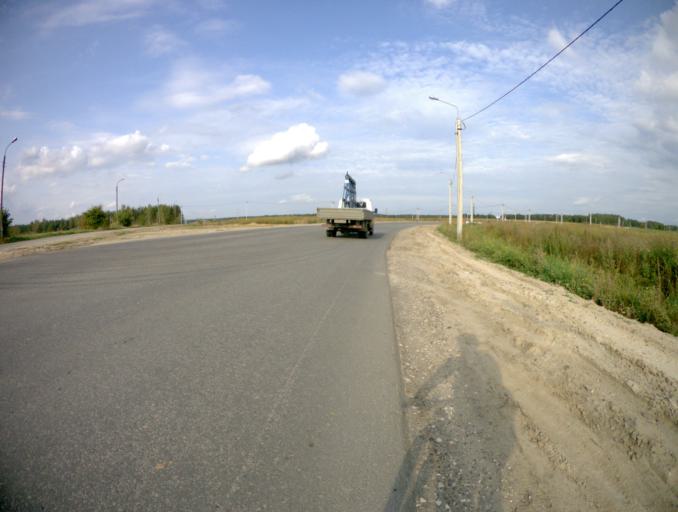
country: RU
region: Vladimir
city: Kommunar
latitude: 56.0704
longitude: 40.4902
